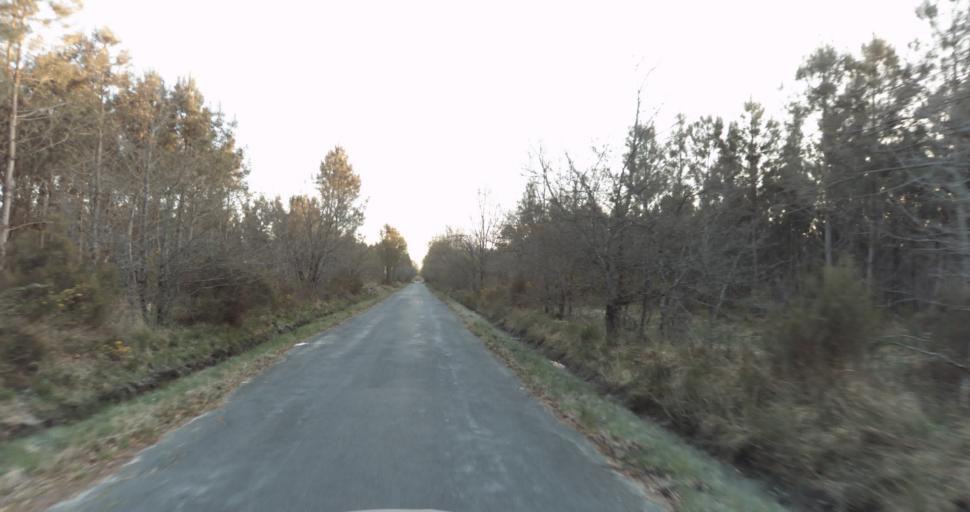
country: FR
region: Aquitaine
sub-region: Departement de la Gironde
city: Martignas-sur-Jalle
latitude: 44.8239
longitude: -0.7416
